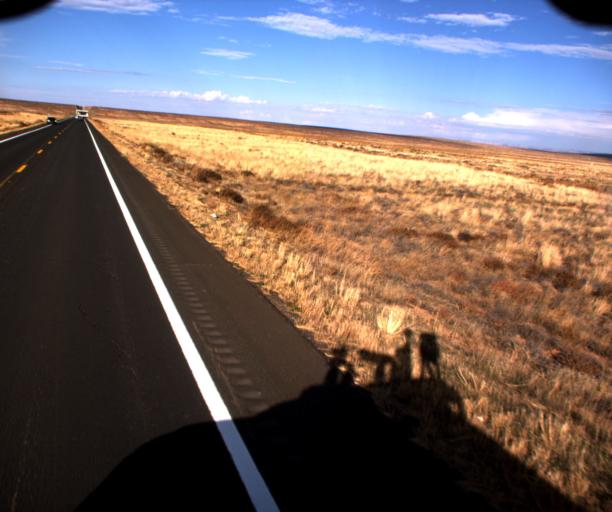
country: US
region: Arizona
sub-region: Apache County
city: Lukachukai
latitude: 36.9621
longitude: -109.4211
